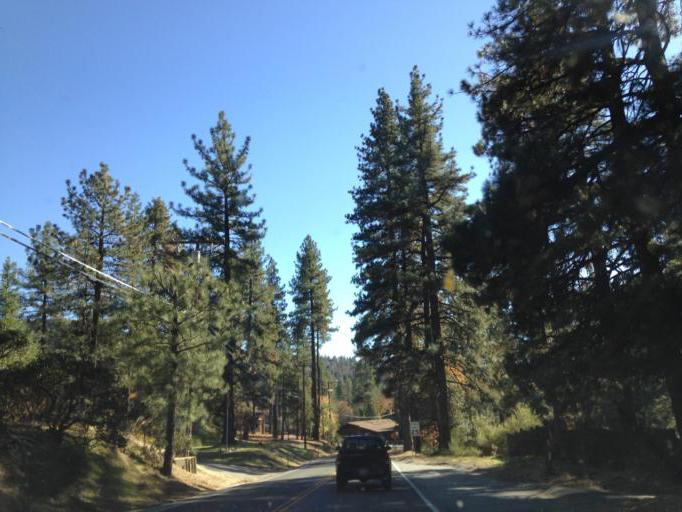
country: US
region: California
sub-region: Riverside County
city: Idyllwild
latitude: 33.7495
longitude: -116.7141
